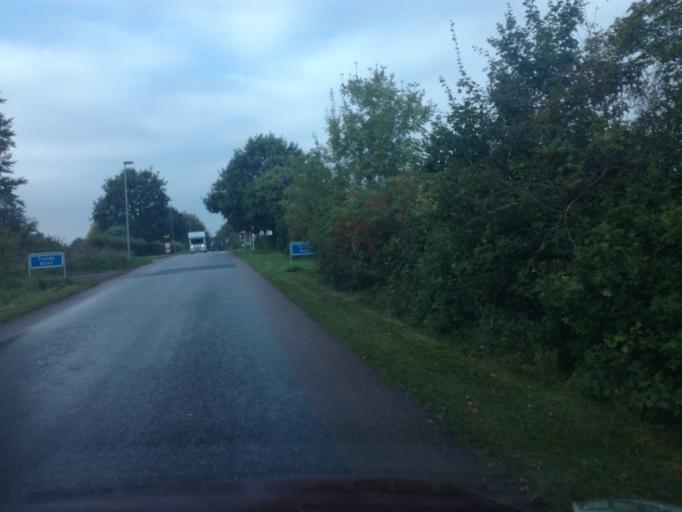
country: DK
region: South Denmark
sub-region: Fredericia Kommune
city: Fredericia
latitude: 55.6244
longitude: 9.8343
